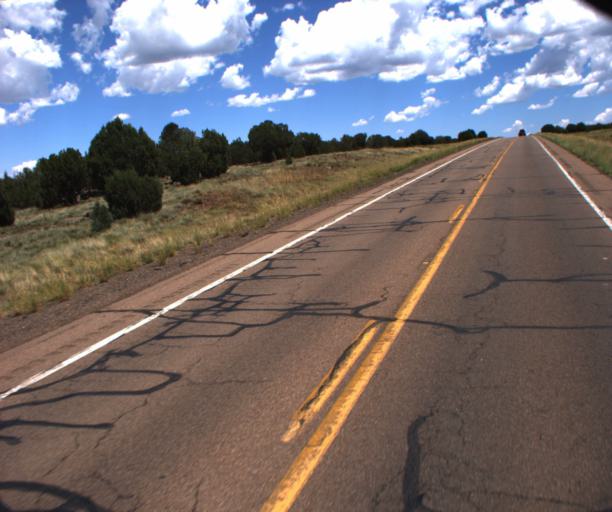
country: US
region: Arizona
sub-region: Navajo County
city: Show Low
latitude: 34.2634
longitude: -109.9683
